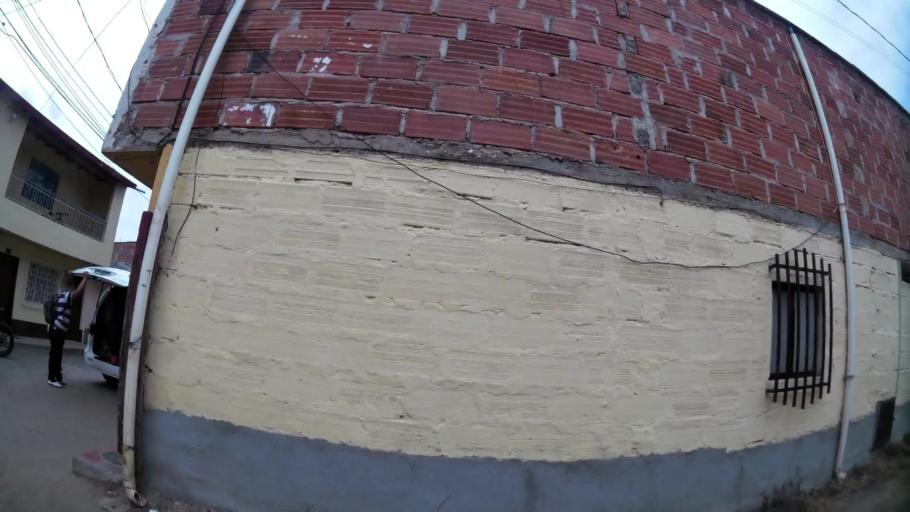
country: CO
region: Antioquia
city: Rionegro
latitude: 6.1571
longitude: -75.3759
